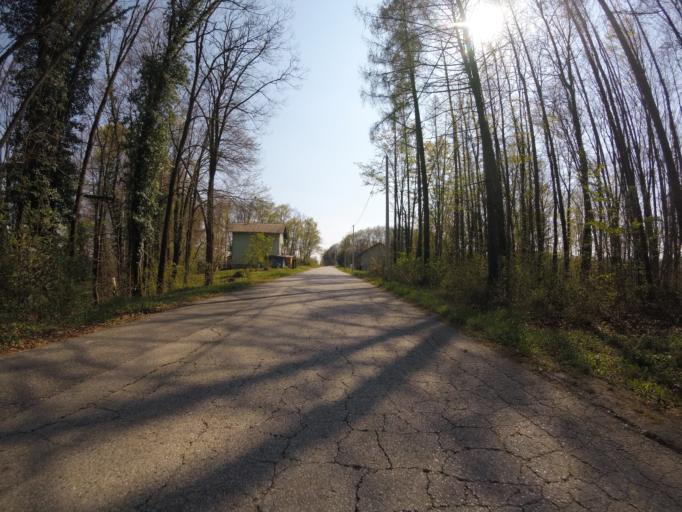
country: HR
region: Grad Zagreb
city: Strmec
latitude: 45.6189
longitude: 15.9497
